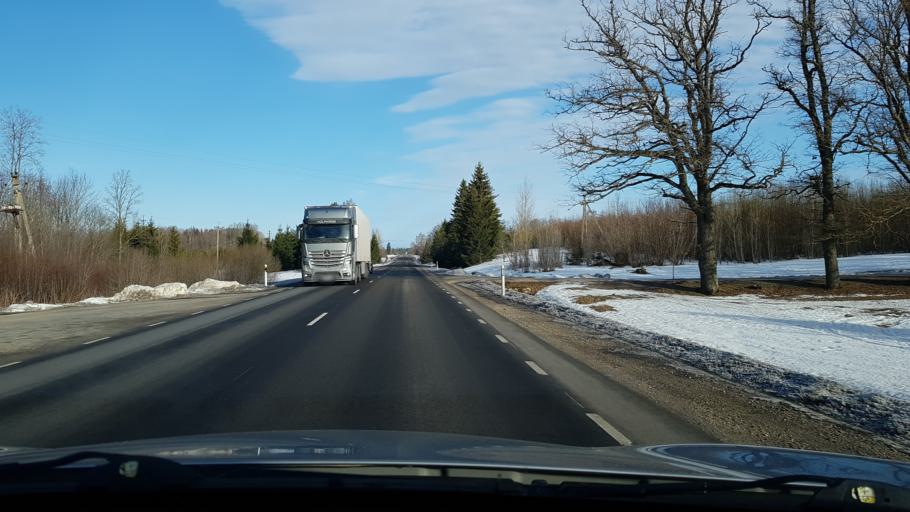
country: EE
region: Viljandimaa
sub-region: Viljandi linn
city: Viljandi
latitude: 58.4082
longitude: 25.5937
